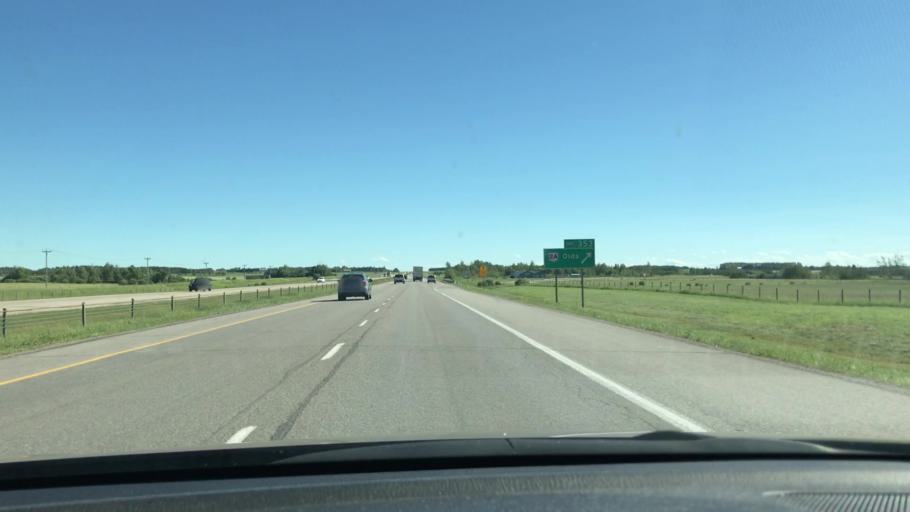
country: CA
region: Alberta
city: Olds
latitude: 51.9118
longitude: -114.0256
